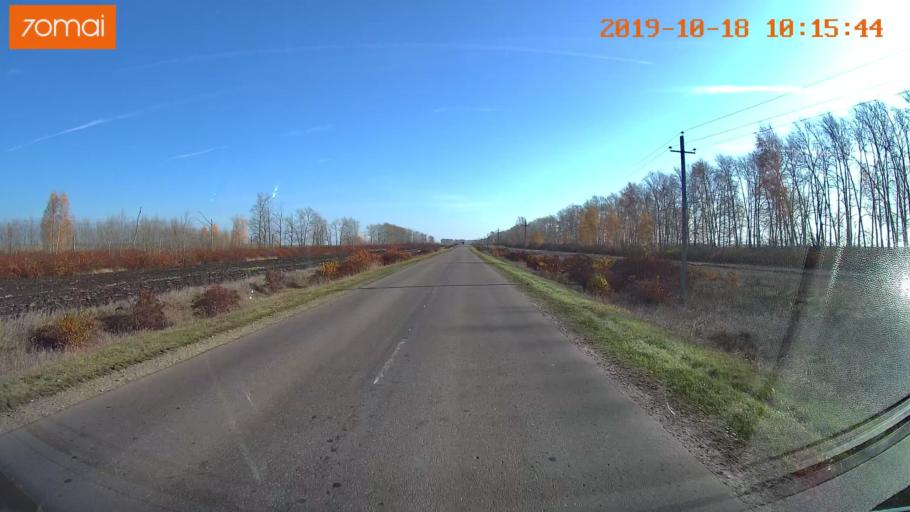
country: RU
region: Tula
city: Kurkino
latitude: 53.4087
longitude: 38.5760
